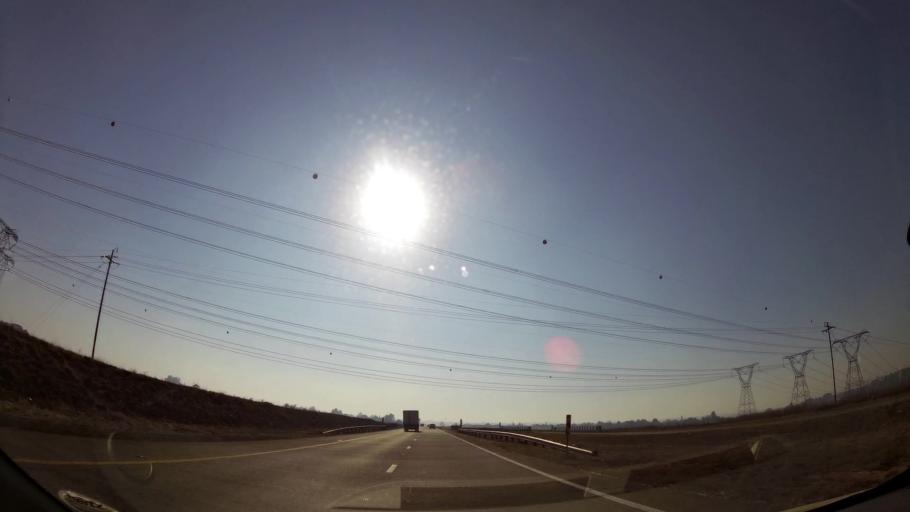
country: ZA
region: Mpumalanga
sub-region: Nkangala District Municipality
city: Witbank
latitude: -25.9339
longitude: 29.2122
